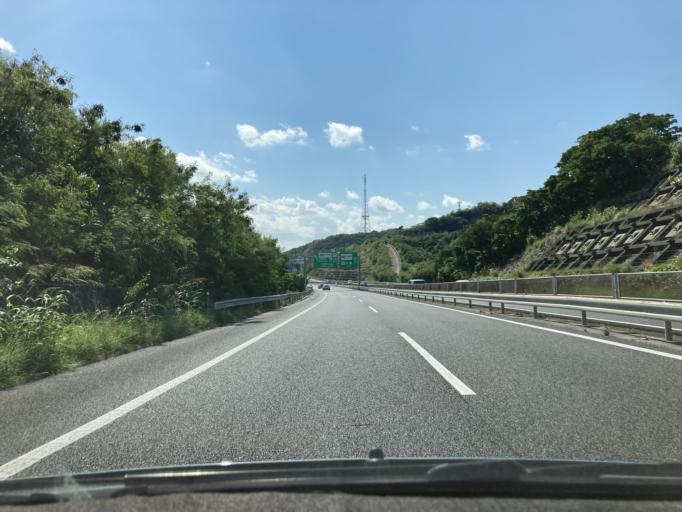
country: JP
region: Okinawa
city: Ginowan
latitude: 26.2260
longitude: 127.7383
